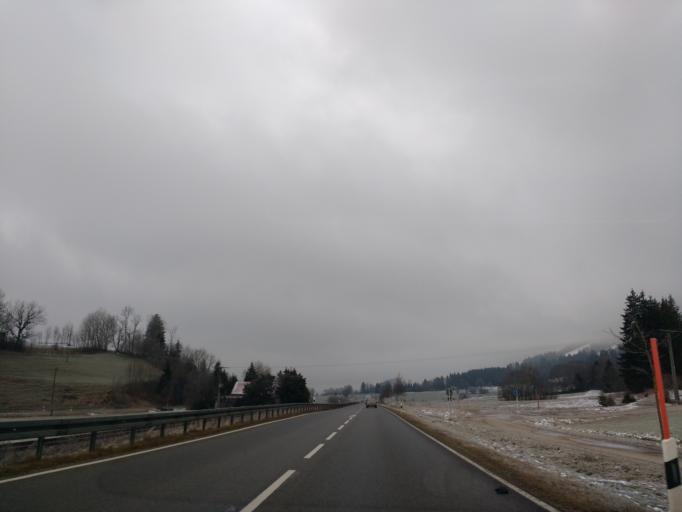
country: DE
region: Bavaria
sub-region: Swabia
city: Nesselwang
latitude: 47.6136
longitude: 10.5207
